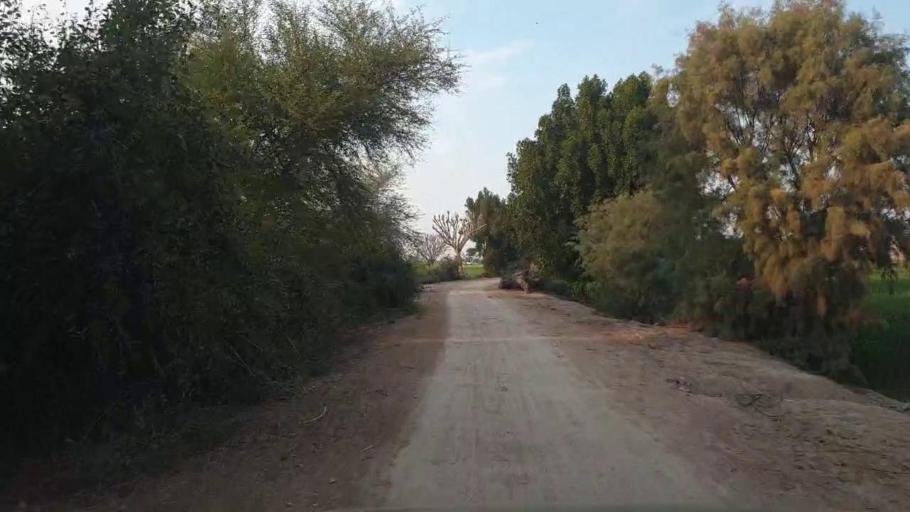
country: PK
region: Sindh
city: Shahpur Chakar
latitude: 26.1609
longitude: 68.6255
